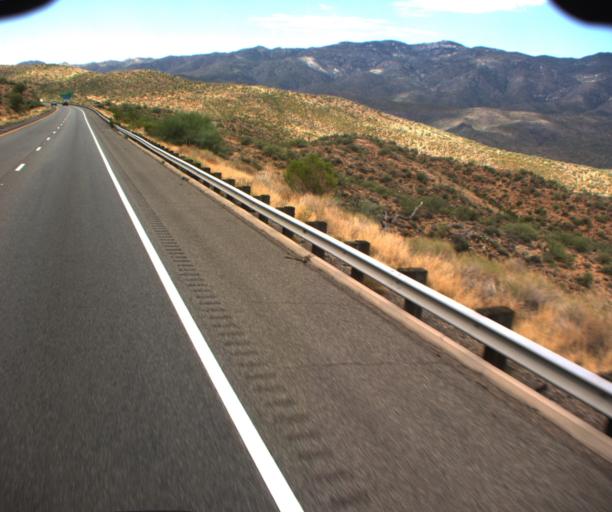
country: US
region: Arizona
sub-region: Yavapai County
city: Black Canyon City
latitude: 34.1525
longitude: -112.1473
